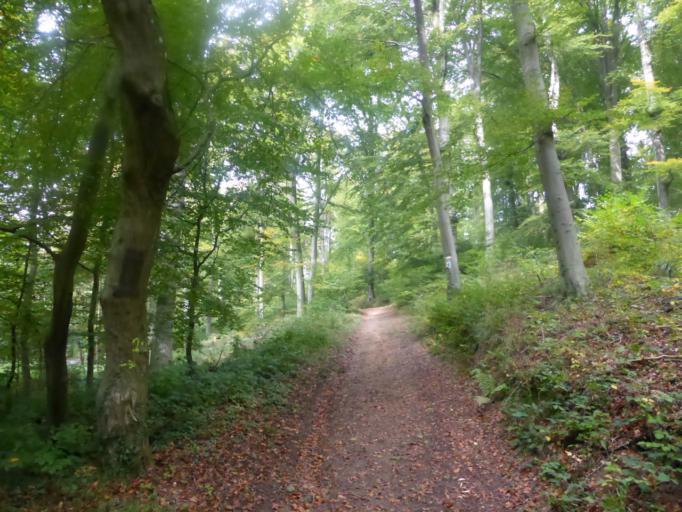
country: LU
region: Luxembourg
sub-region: Canton de Luxembourg
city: Hesperange
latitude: 49.5806
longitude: 6.1520
